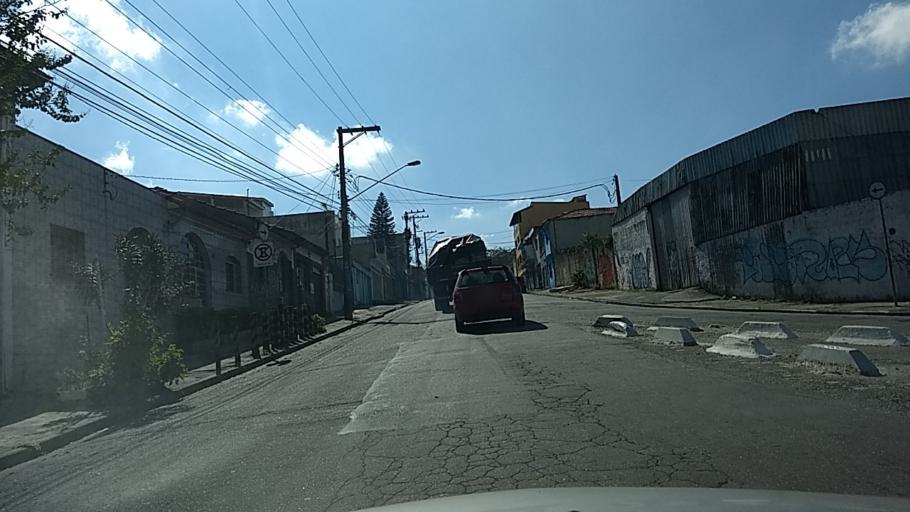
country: BR
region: Sao Paulo
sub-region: Sao Paulo
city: Sao Paulo
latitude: -23.5174
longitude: -46.5834
